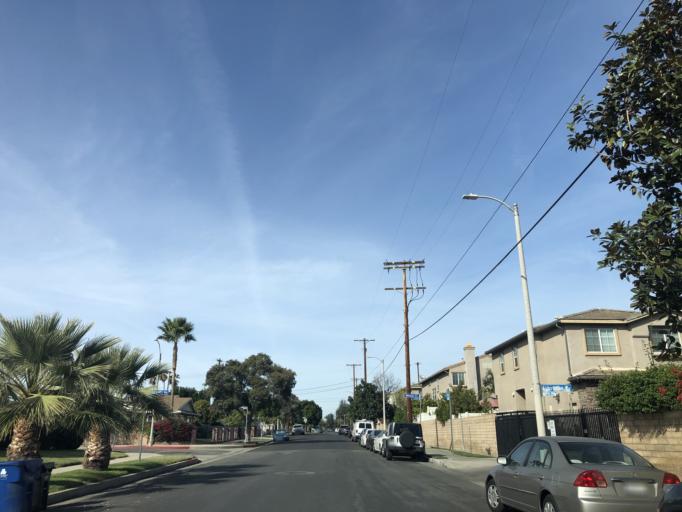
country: US
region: California
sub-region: Los Angeles County
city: San Fernando
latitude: 34.2414
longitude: -118.4169
